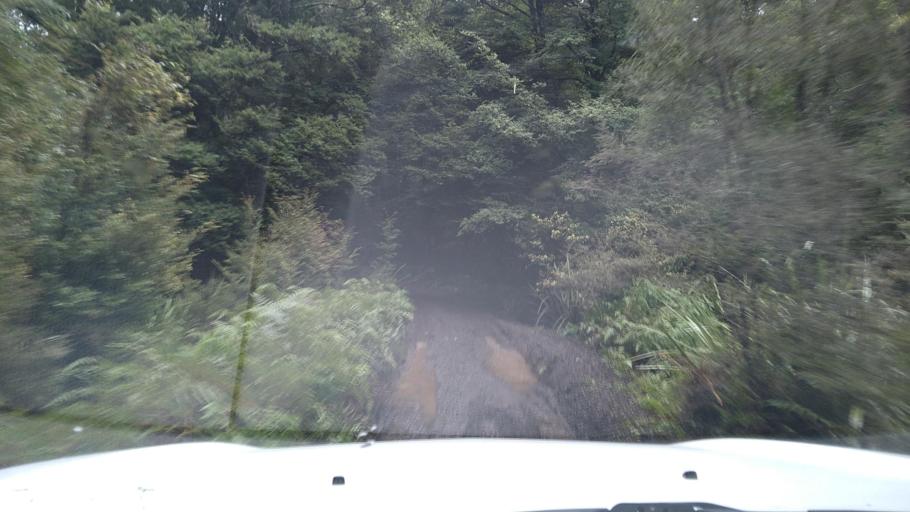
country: NZ
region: Manawatu-Wanganui
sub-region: Ruapehu District
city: Waiouru
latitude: -39.3859
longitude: 175.4987
